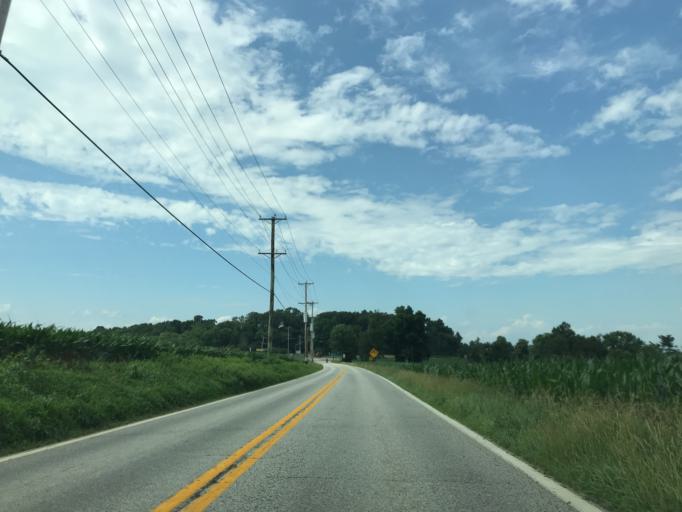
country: US
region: Maryland
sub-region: Harford County
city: Jarrettsville
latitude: 39.6695
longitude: -76.4084
